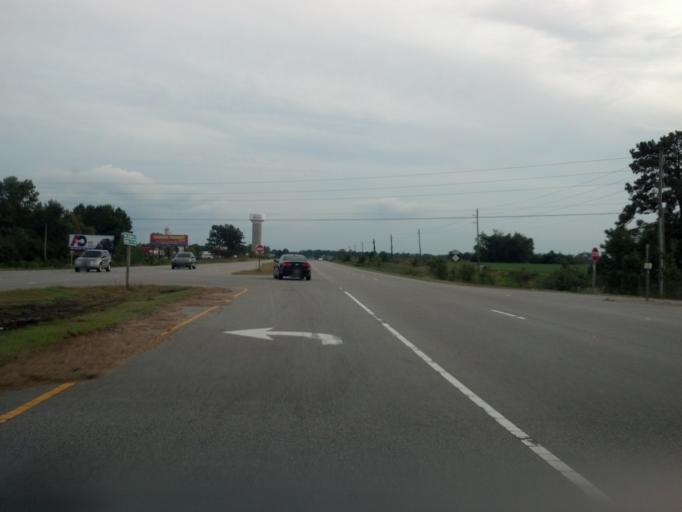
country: US
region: North Carolina
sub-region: Pitt County
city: Ayden
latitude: 35.4924
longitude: -77.4285
